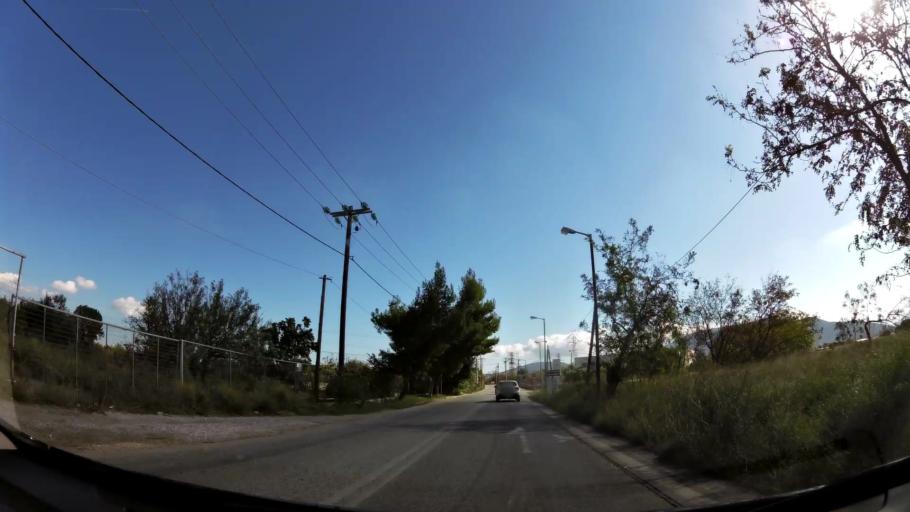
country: GR
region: Attica
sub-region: Nomarchia Anatolikis Attikis
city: Markopoulo
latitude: 37.8857
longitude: 23.9162
